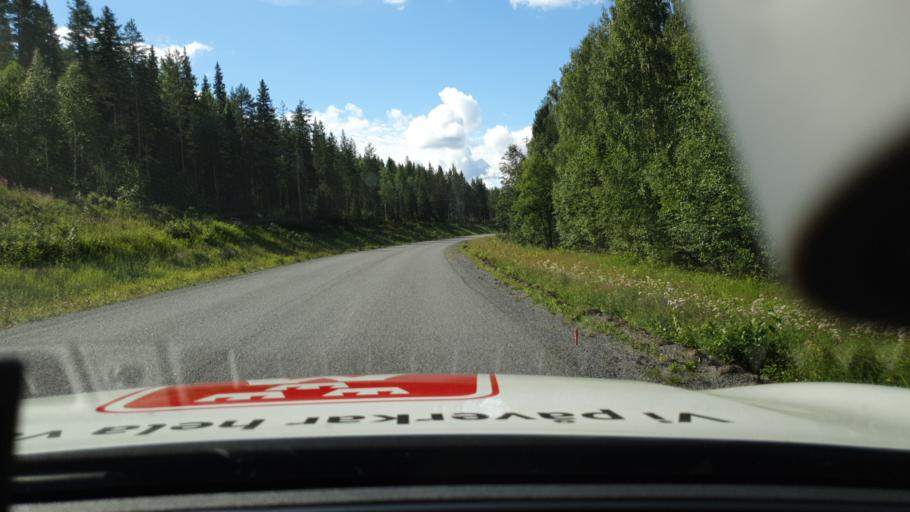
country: SE
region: Norrbotten
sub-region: Bodens Kommun
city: Boden
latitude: 65.9421
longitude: 21.8273
